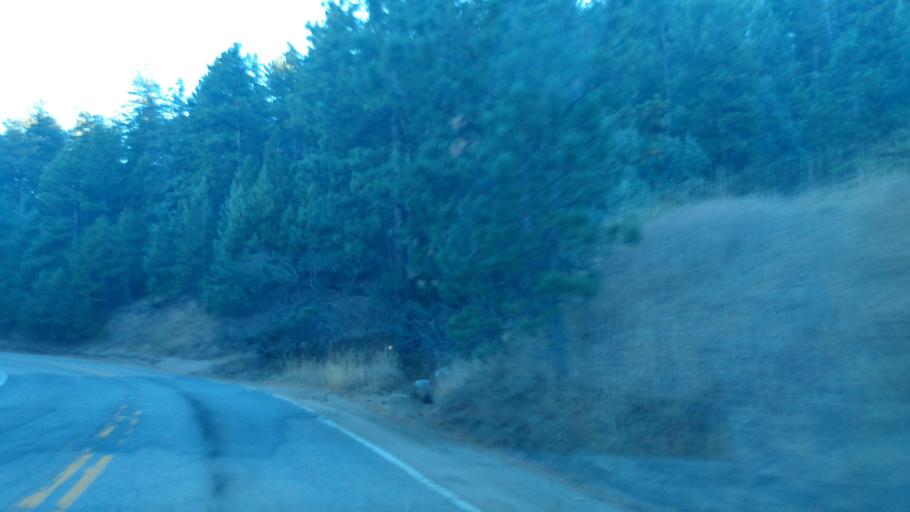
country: US
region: Colorado
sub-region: Boulder County
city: Boulder
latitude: 39.9994
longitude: -105.3564
